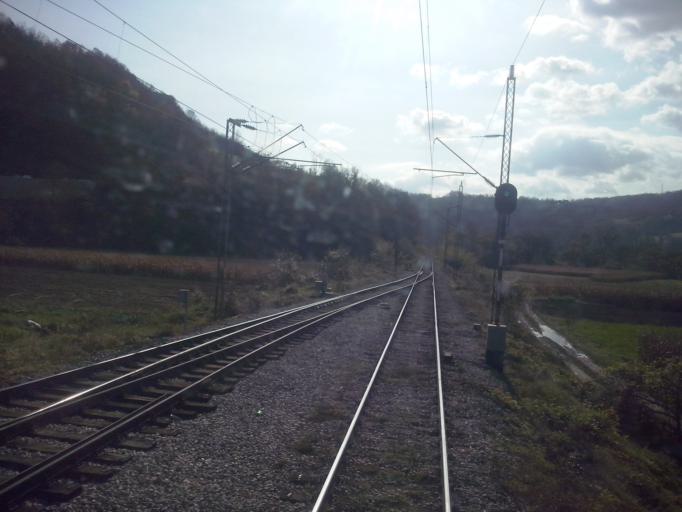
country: RS
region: Central Serbia
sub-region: Zlatiborski Okrug
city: Pozega
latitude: 43.9248
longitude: 19.9901
